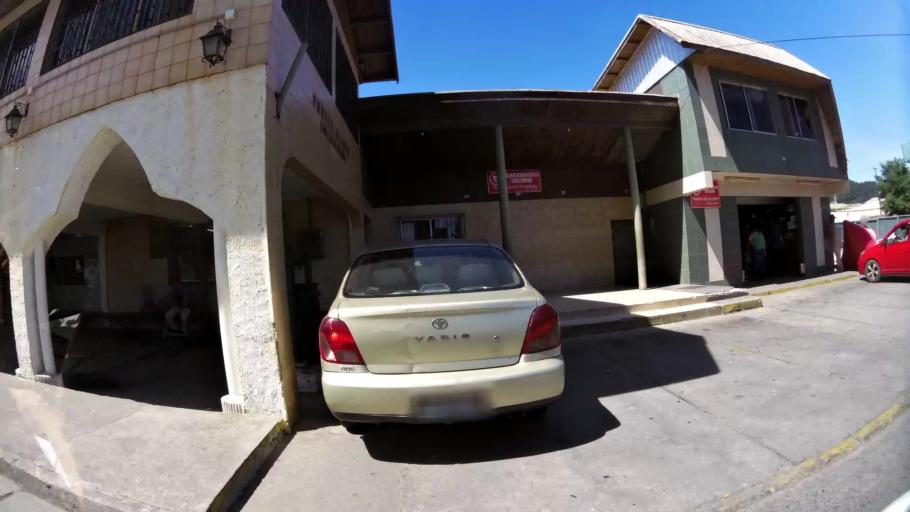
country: CL
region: Biobio
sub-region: Provincia de Concepcion
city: Penco
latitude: -36.7370
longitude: -72.9955
